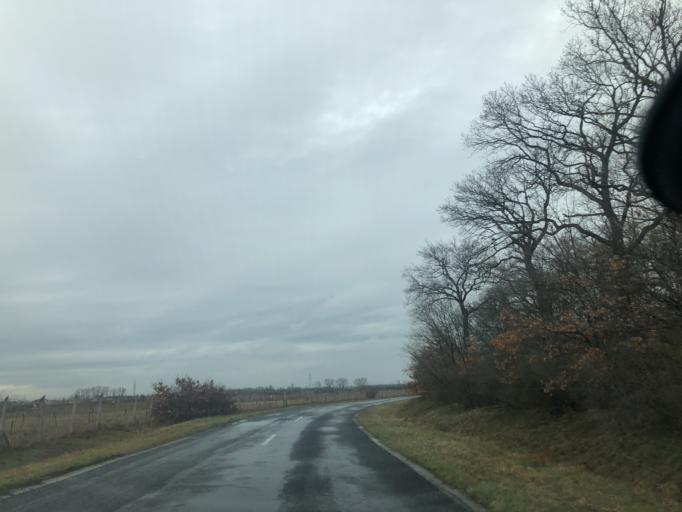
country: HU
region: Gyor-Moson-Sopron
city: Fertoszentmiklos
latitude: 47.5921
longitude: 16.9508
